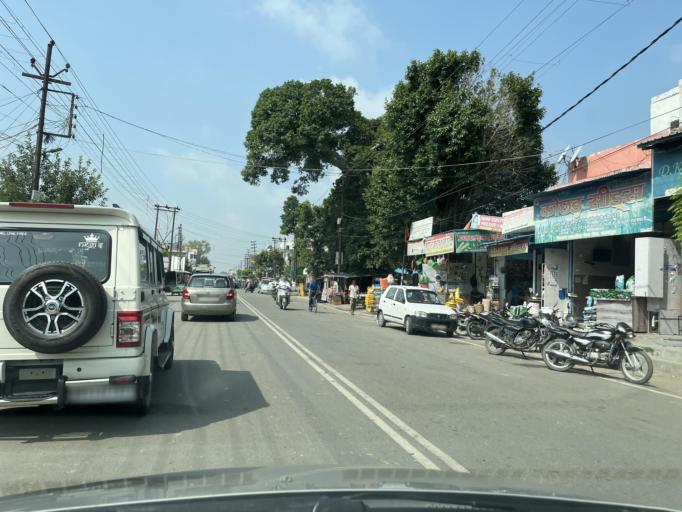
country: IN
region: Uttarakhand
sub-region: Udham Singh Nagar
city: Bazpur
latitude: 29.1622
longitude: 79.1554
